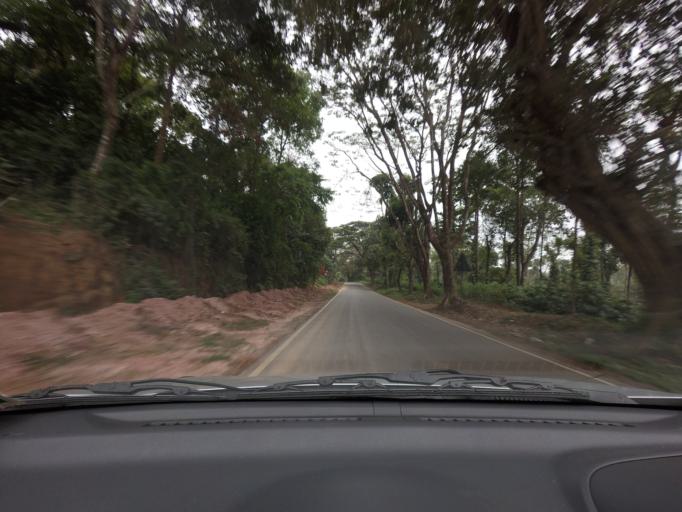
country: IN
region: Karnataka
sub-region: Hassan
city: Sakleshpur
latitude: 12.9565
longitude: 75.7457
